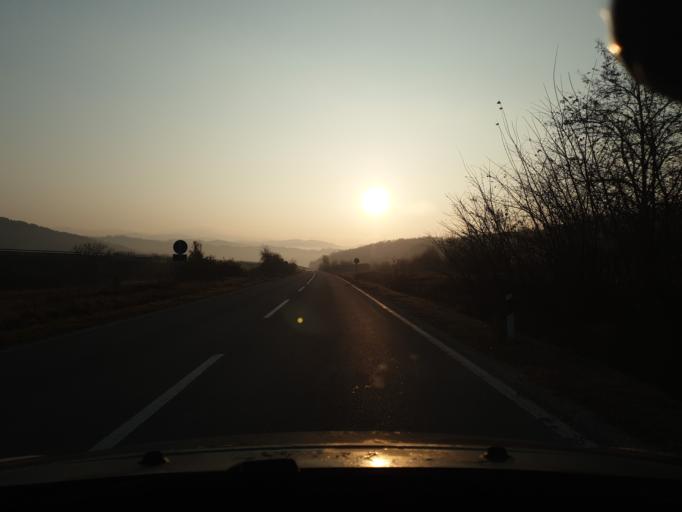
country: RS
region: Central Serbia
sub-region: Jablanicki Okrug
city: Vlasotince
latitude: 42.9155
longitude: 22.0328
